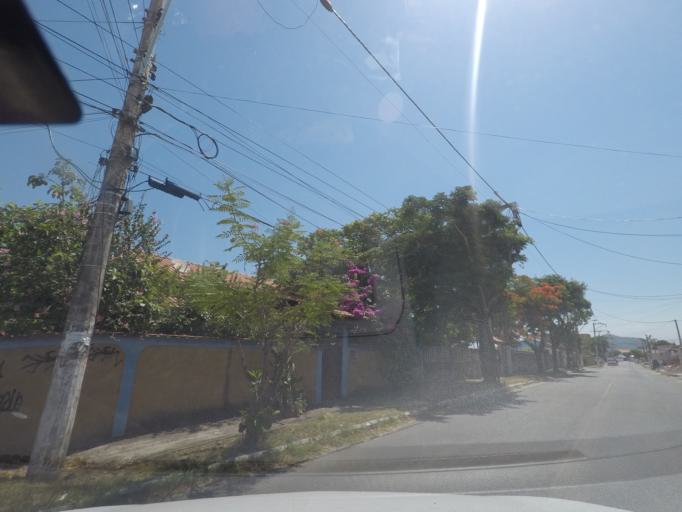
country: BR
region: Rio de Janeiro
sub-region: Marica
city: Marica
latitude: -22.9671
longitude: -42.9595
